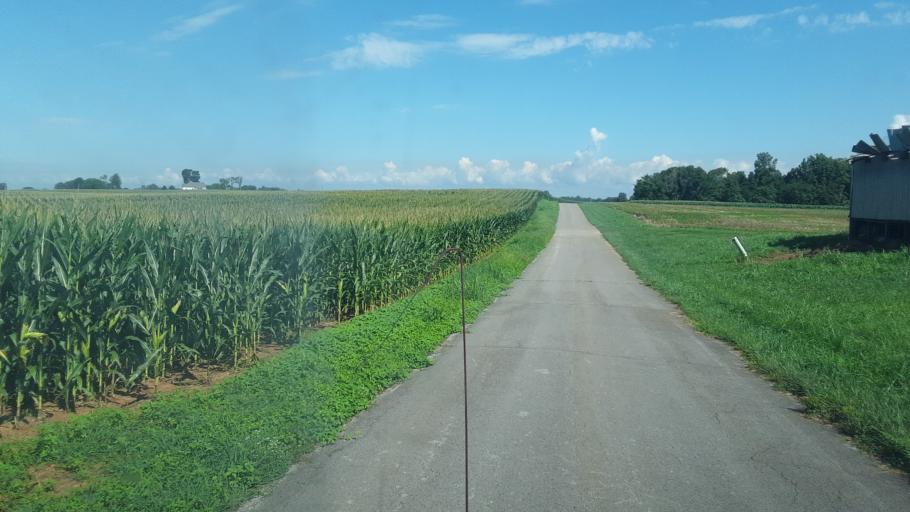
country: US
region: Kentucky
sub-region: Todd County
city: Elkton
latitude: 36.7719
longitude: -87.2300
